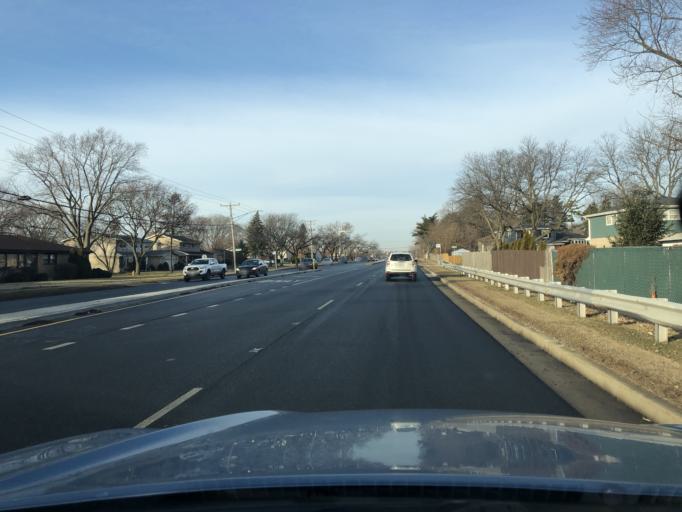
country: US
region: Illinois
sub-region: Cook County
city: Mount Prospect
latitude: 42.0476
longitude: -87.9549
